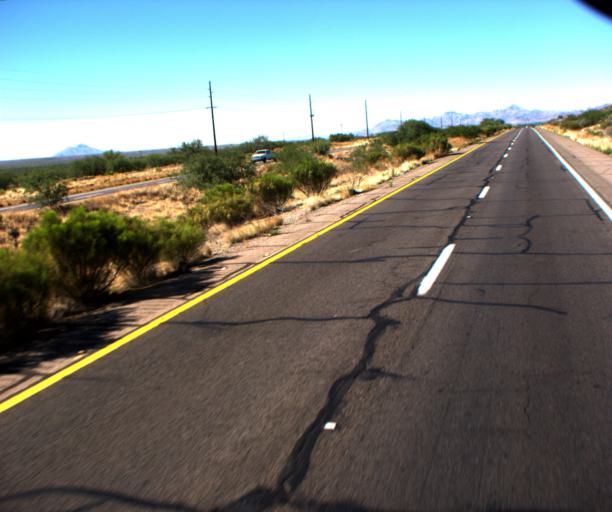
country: US
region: Arizona
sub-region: Pima County
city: Arivaca Junction
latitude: 31.7603
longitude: -111.0389
